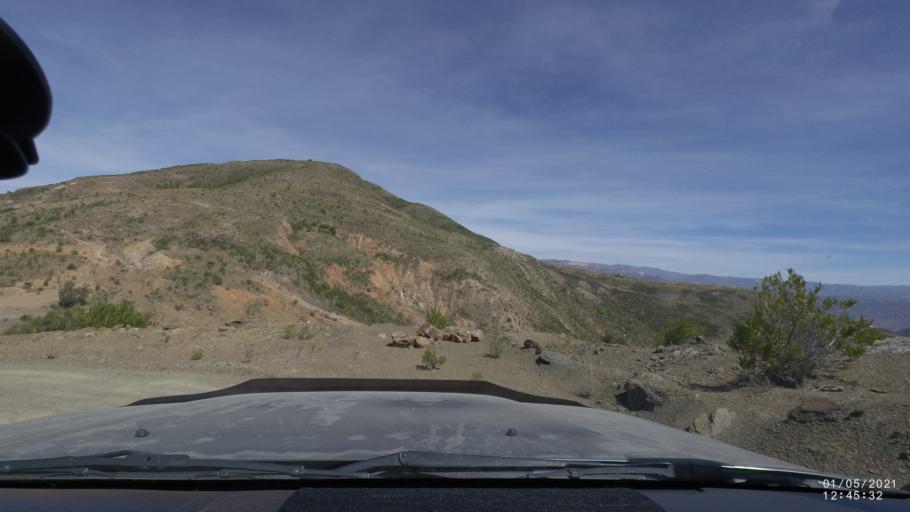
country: BO
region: Cochabamba
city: Capinota
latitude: -17.6873
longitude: -66.1593
